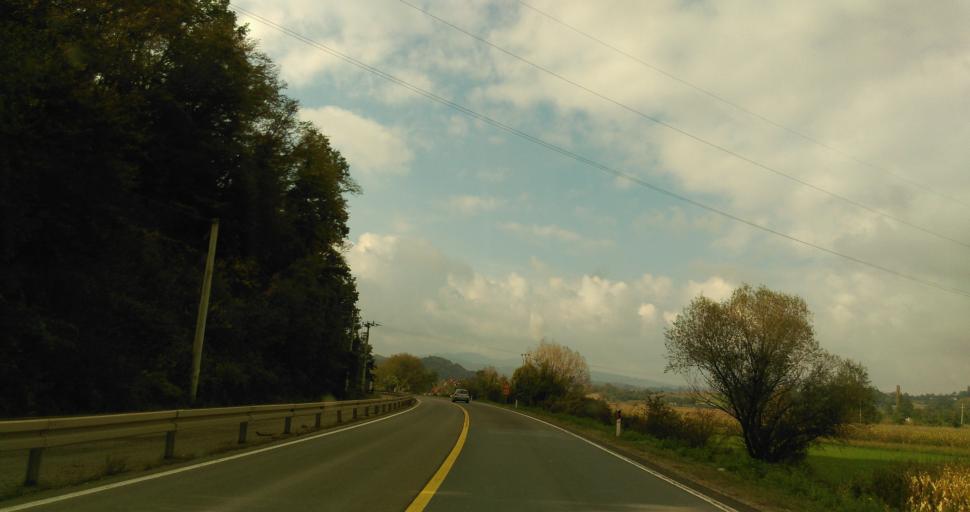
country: RS
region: Central Serbia
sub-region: Kolubarski Okrug
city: Ljig
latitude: 44.2397
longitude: 20.2665
